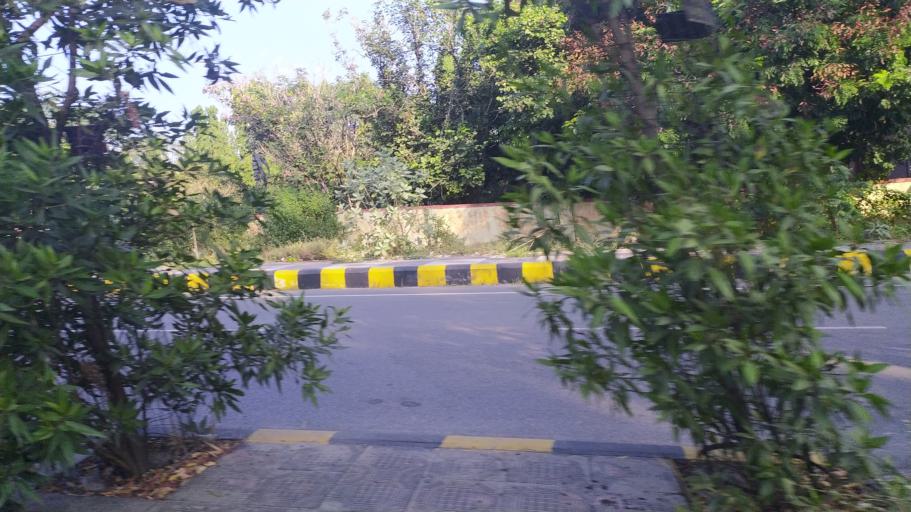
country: IN
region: Telangana
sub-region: Hyderabad
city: Hyderabad
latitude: 17.3197
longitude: 78.3937
